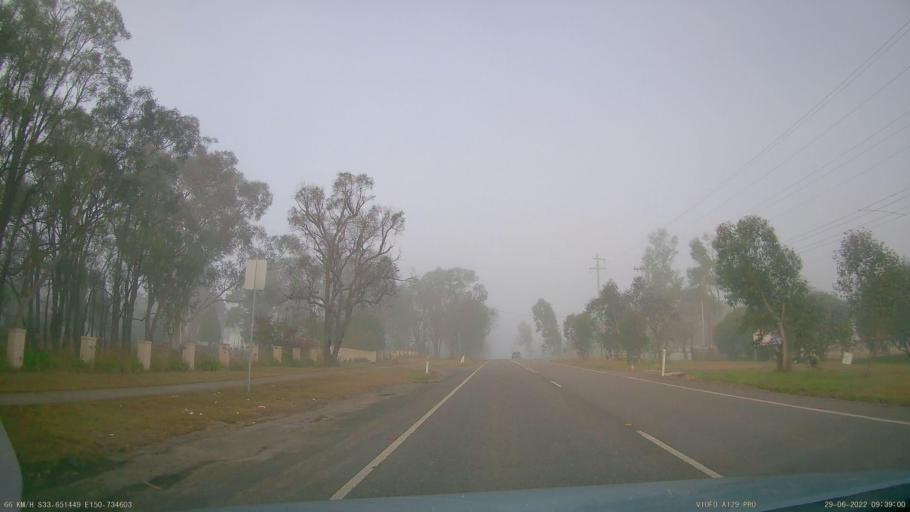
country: AU
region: New South Wales
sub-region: Hawkesbury
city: Richmond
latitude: -33.6519
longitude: 150.7345
